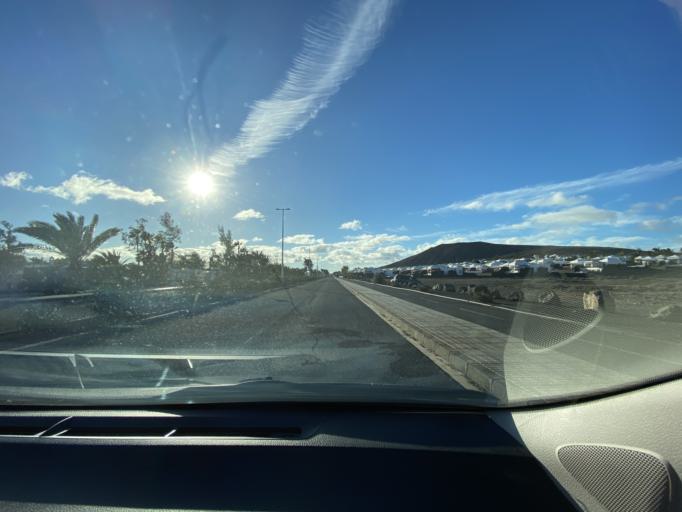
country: ES
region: Canary Islands
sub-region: Provincia de Las Palmas
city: Playa Blanca
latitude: 28.8664
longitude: -13.8394
